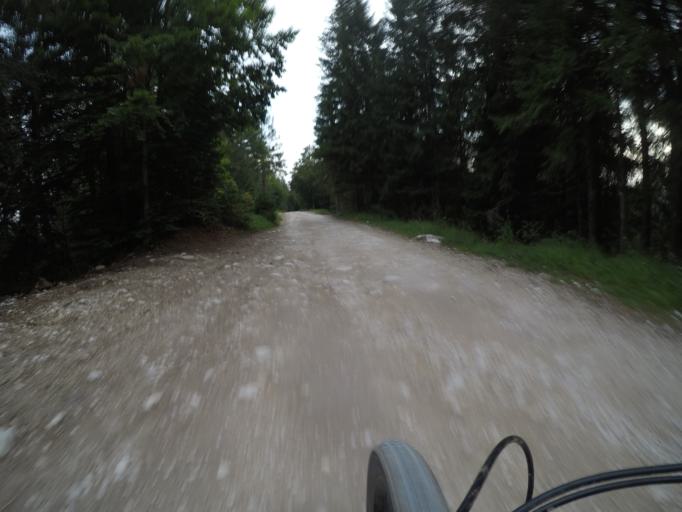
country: IT
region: Veneto
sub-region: Provincia di Vicenza
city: Gallio
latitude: 45.9034
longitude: 11.5256
